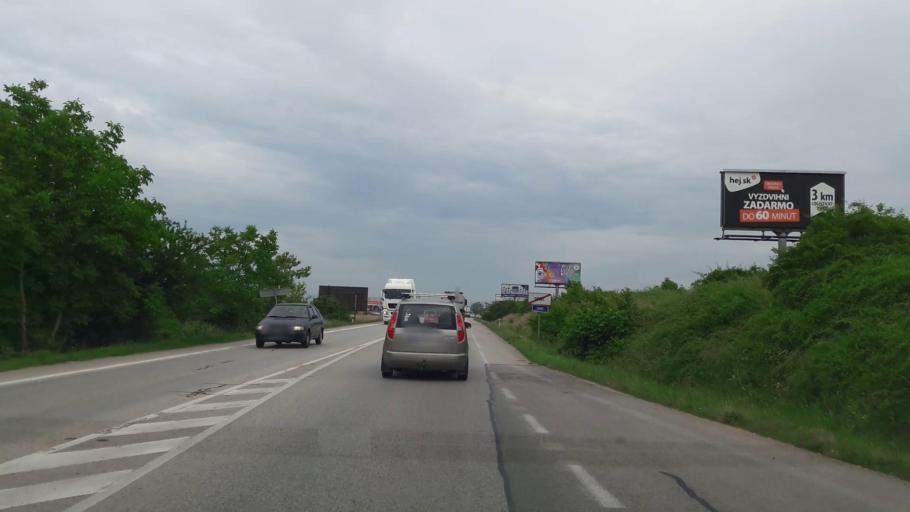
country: SK
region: Bratislavsky
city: Senec
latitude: 48.2246
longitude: 17.3829
